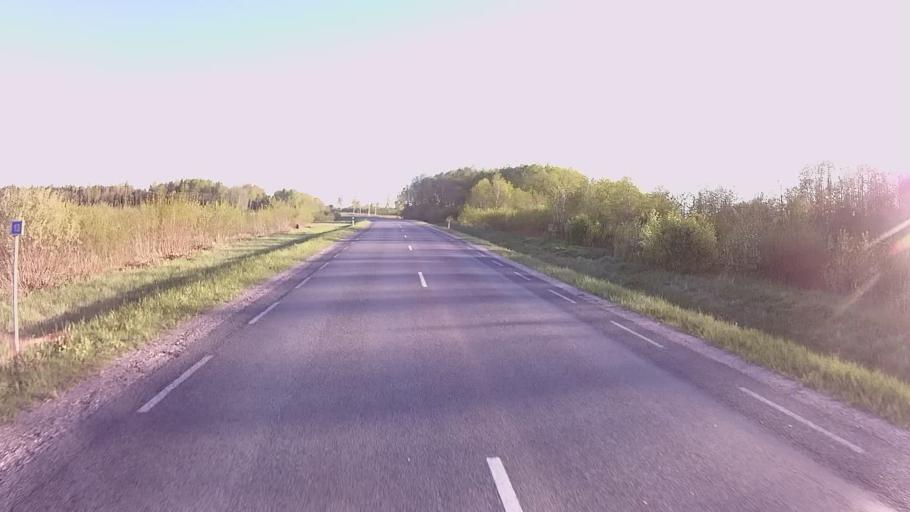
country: EE
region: Viljandimaa
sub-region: Viiratsi vald
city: Viiratsi
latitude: 58.4566
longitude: 25.7466
